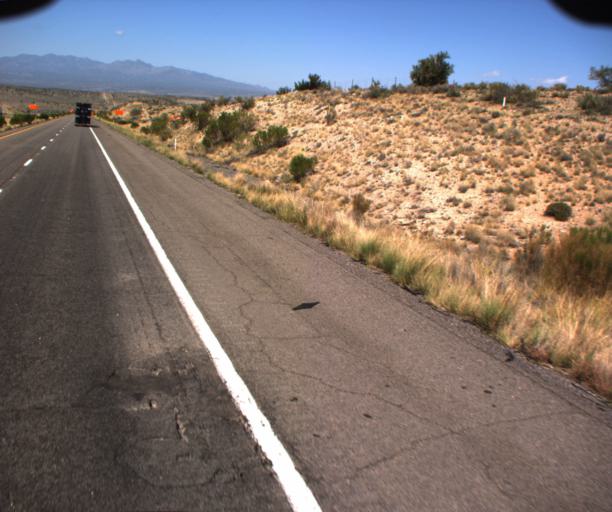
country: US
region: Arizona
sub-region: Mohave County
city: Peach Springs
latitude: 35.1605
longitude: -113.5499
